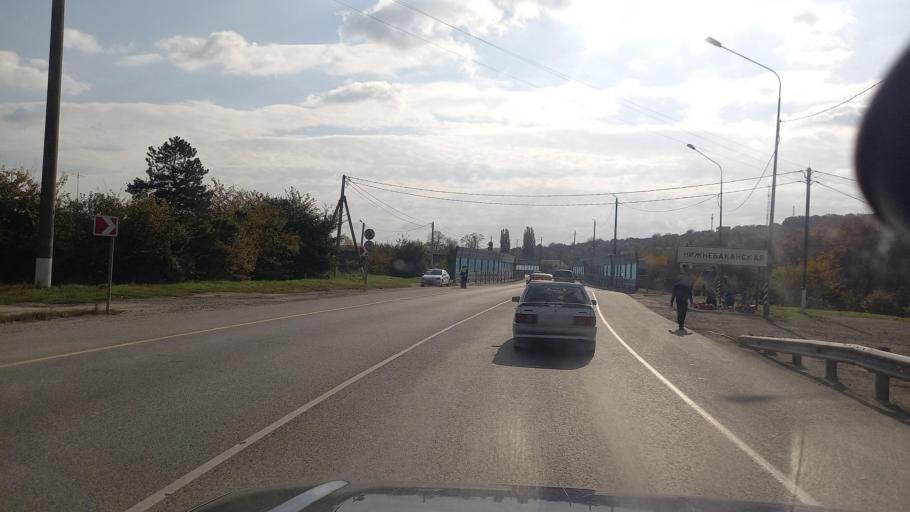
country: RU
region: Krasnodarskiy
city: Krymsk
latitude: 44.8709
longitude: 37.8428
